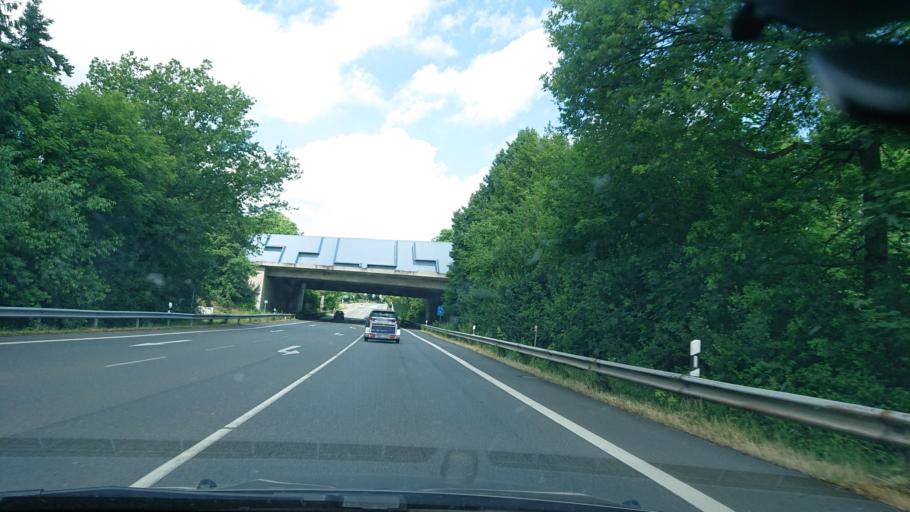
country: DE
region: North Rhine-Westphalia
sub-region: Regierungsbezirk Detmold
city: Hiddenhausen
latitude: 52.1786
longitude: 8.6134
